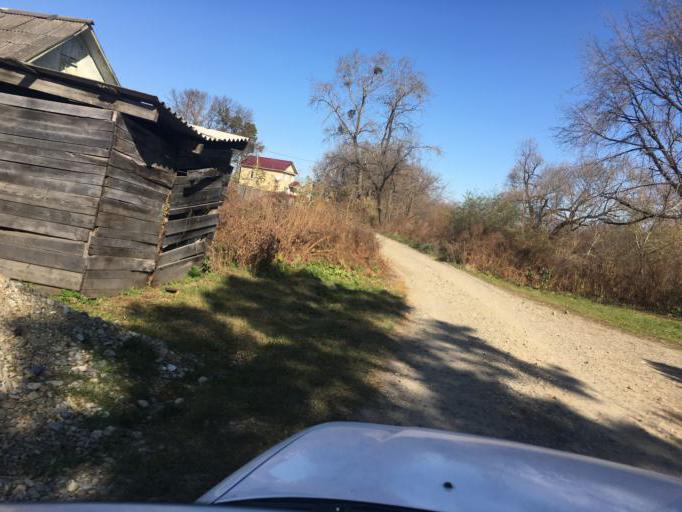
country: RU
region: Primorskiy
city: Dal'nerechensk
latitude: 45.9092
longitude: 133.7954
